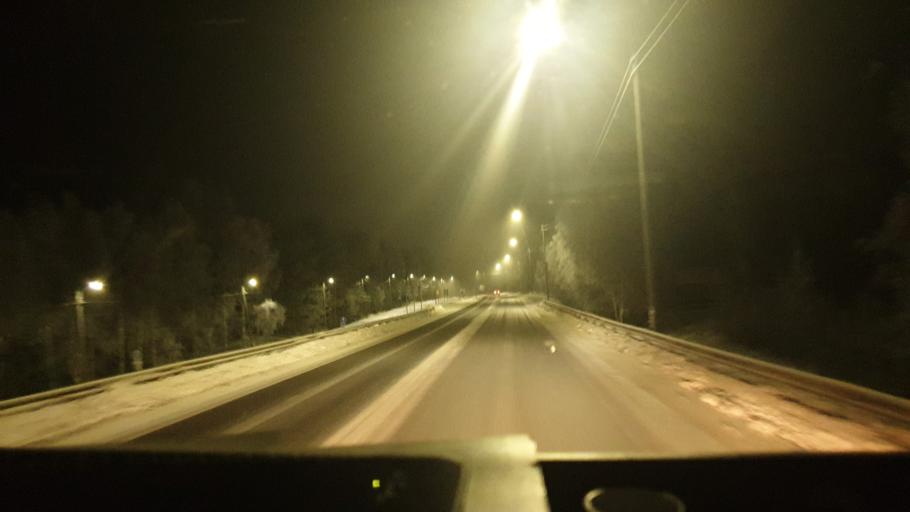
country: FI
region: Northern Ostrobothnia
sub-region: Oulunkaari
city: Ii
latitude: 65.3409
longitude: 25.3681
